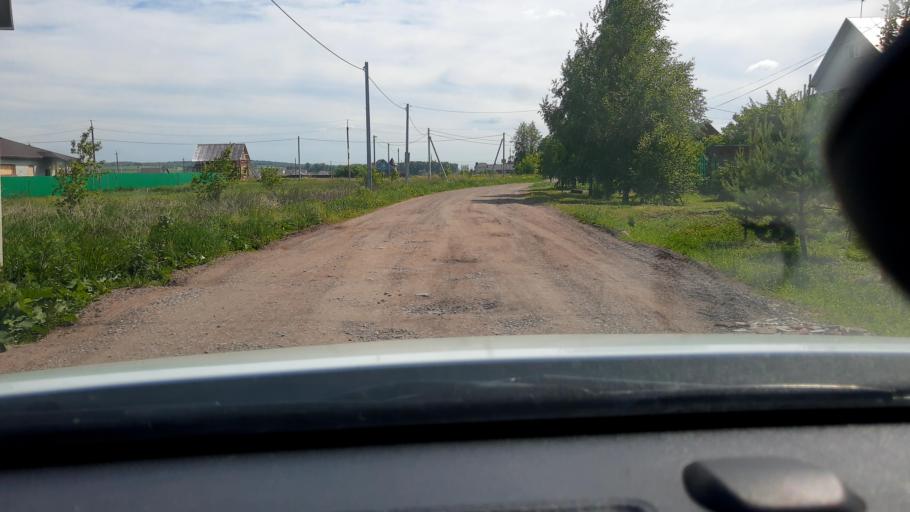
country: RU
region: Bashkortostan
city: Avdon
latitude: 54.4469
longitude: 55.8191
